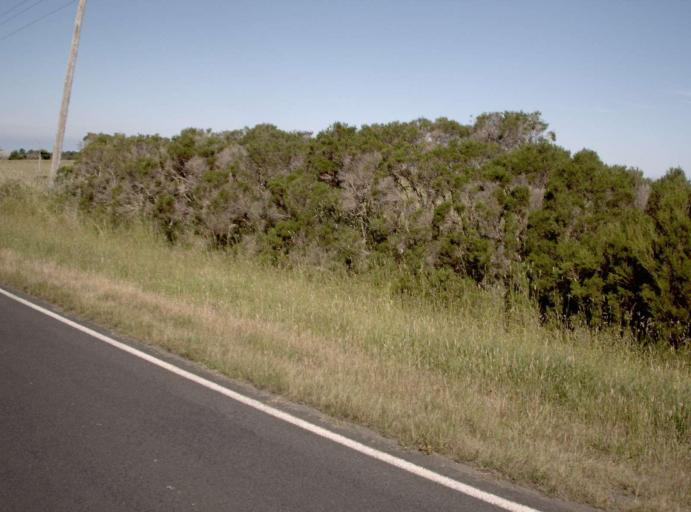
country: AU
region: Victoria
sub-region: Latrobe
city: Traralgon
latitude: -38.6285
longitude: 146.5991
